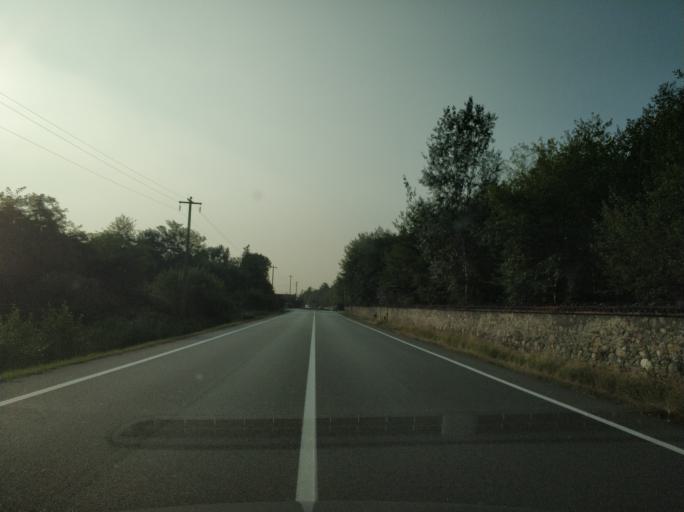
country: IT
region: Piedmont
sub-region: Provincia di Torino
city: Robassomero
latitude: 45.1913
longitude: 7.5652
